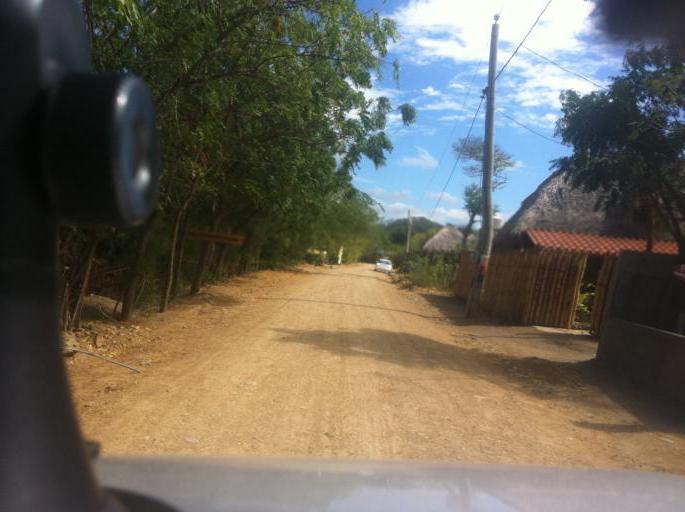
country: NI
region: Rivas
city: Tola
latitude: 11.4758
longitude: -86.1113
